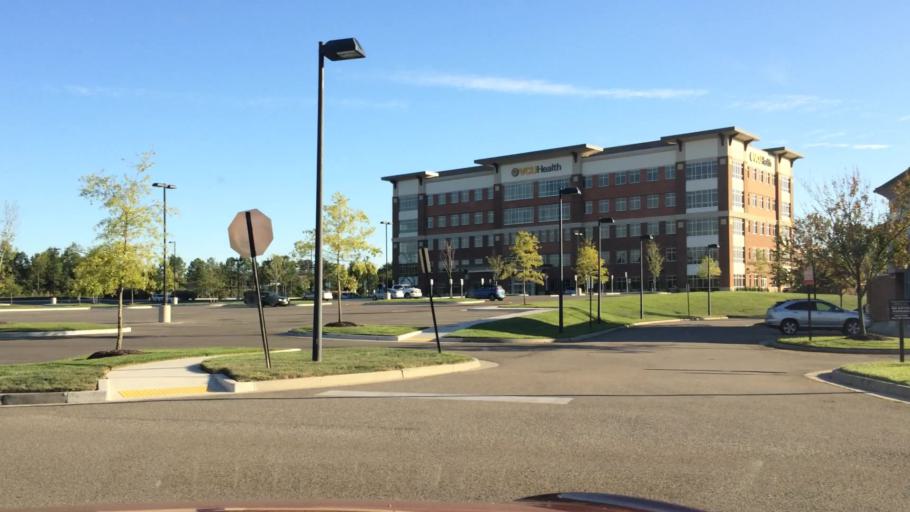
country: US
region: Virginia
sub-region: Henrico County
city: Short Pump
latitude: 37.6588
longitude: -77.6261
